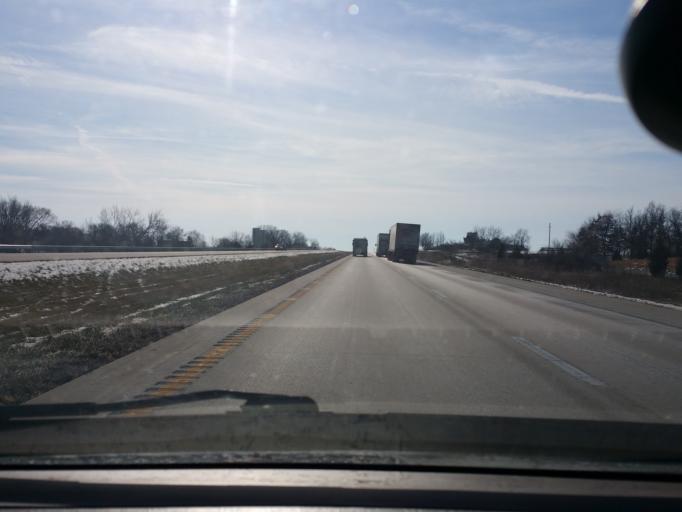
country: US
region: Missouri
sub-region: Clinton County
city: Cameron
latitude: 39.6531
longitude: -94.2395
